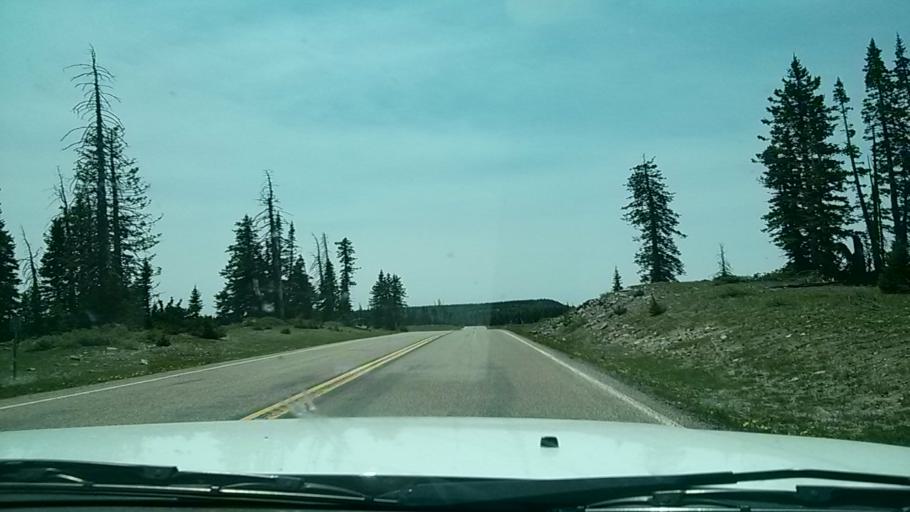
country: US
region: Utah
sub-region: Iron County
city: Cedar City
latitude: 37.5976
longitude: -112.8500
